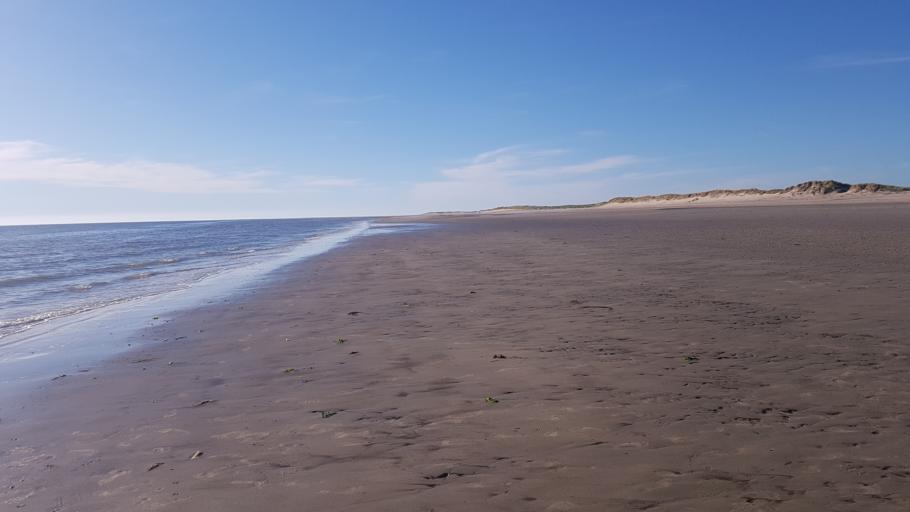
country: DE
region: Schleswig-Holstein
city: List
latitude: 55.0755
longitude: 8.4847
